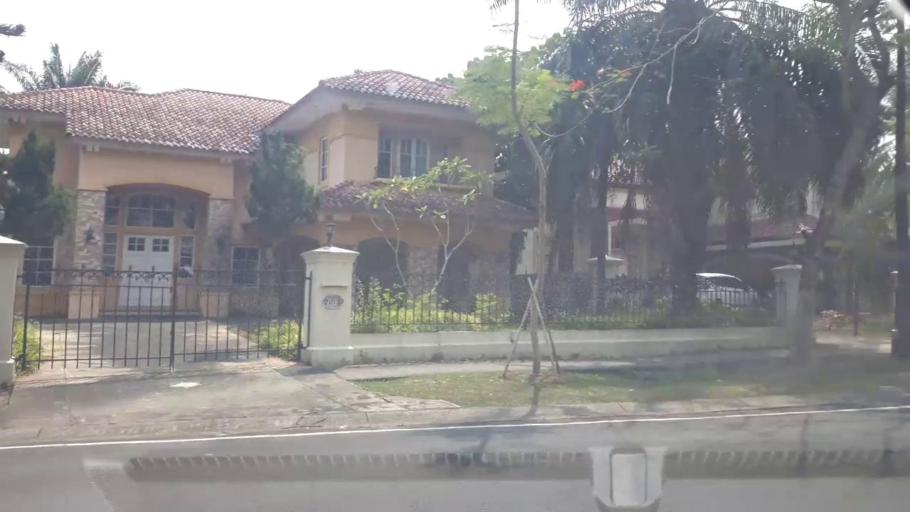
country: ID
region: Banten
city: Curug
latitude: -6.2394
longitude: 106.5954
